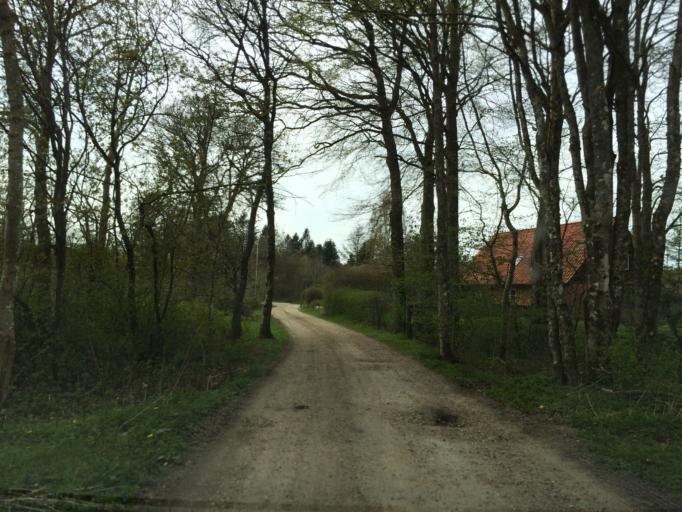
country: DK
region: Central Jutland
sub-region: Holstebro Kommune
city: Ulfborg
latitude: 56.2224
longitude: 8.4725
